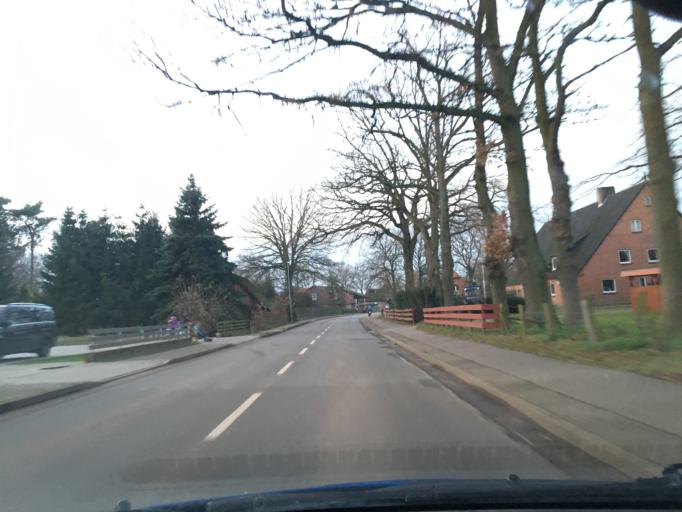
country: DE
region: Lower Saxony
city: Barum
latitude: 53.3484
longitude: 10.4145
